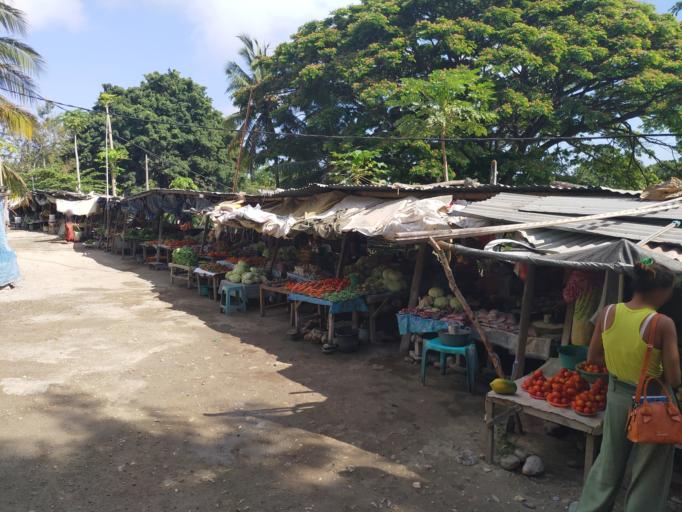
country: TL
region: Baucau
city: Baucau
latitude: -8.4614
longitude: 126.4514
